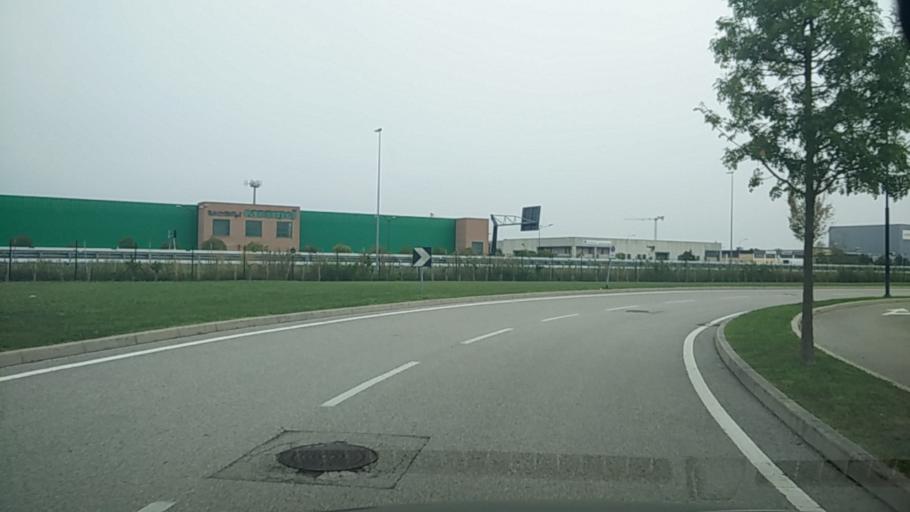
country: IT
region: Veneto
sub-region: Provincia di Venezia
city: Noventa di Piave
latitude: 45.6715
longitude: 12.5333
